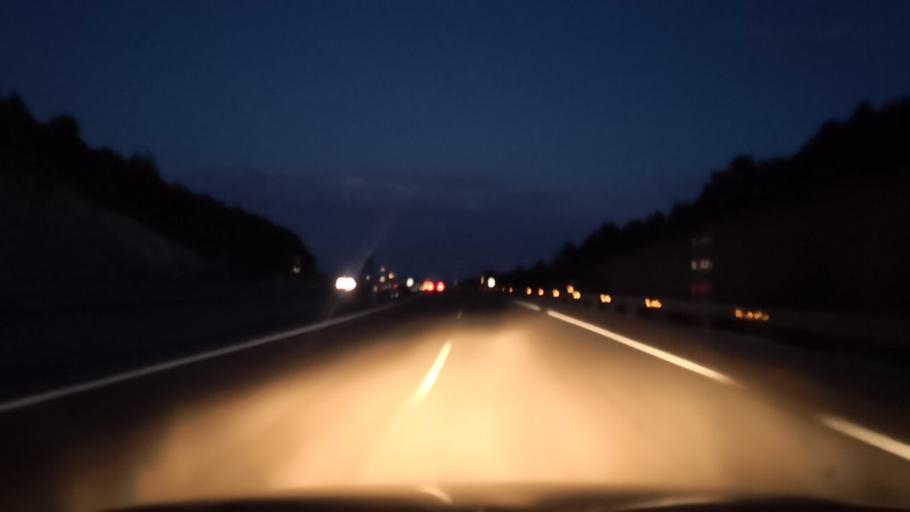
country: ES
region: Castille and Leon
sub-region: Provincia de Leon
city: Villagaton
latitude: 42.5655
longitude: -6.2113
